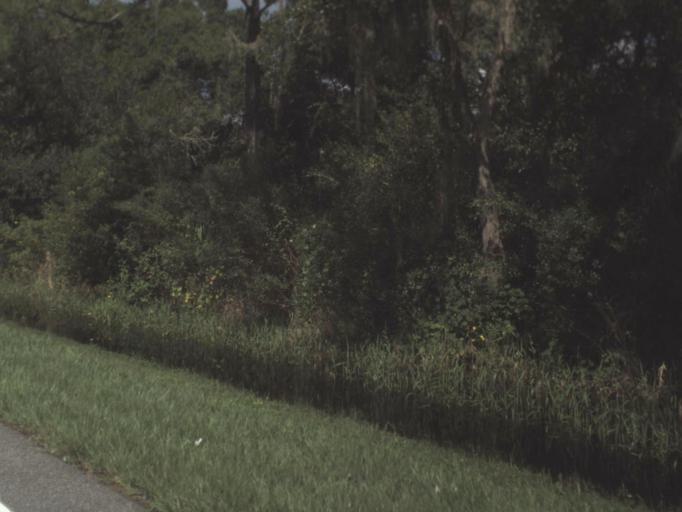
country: US
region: Florida
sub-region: Sarasota County
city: Warm Mineral Springs
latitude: 27.1957
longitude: -82.2129
